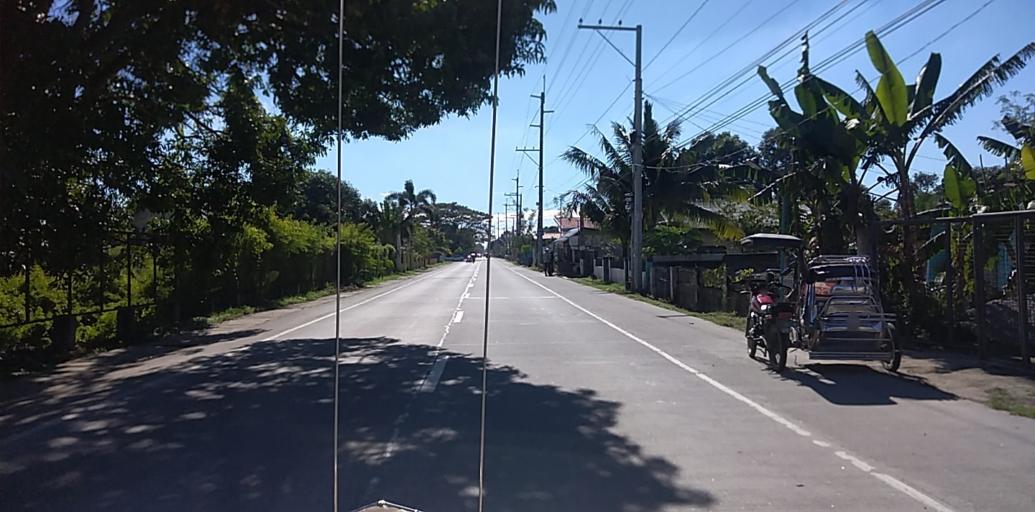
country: PH
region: Central Luzon
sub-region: Province of Pampanga
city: Santo Domingo
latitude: 15.0626
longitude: 120.7709
